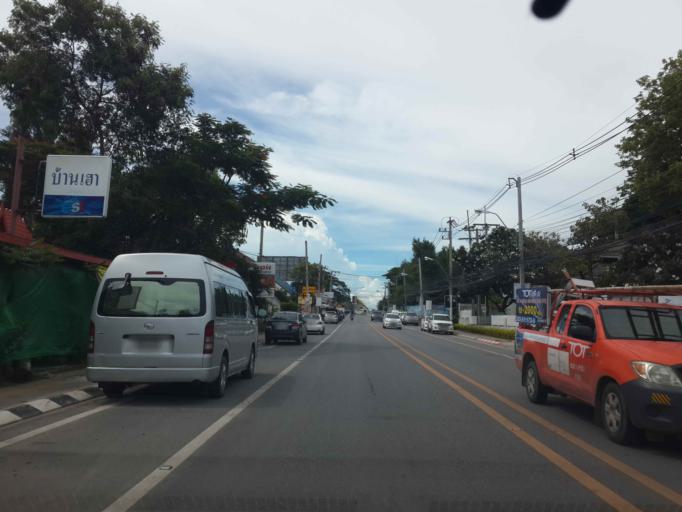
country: TH
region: Prachuap Khiri Khan
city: Hua Hin
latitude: 12.5318
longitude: 99.9661
